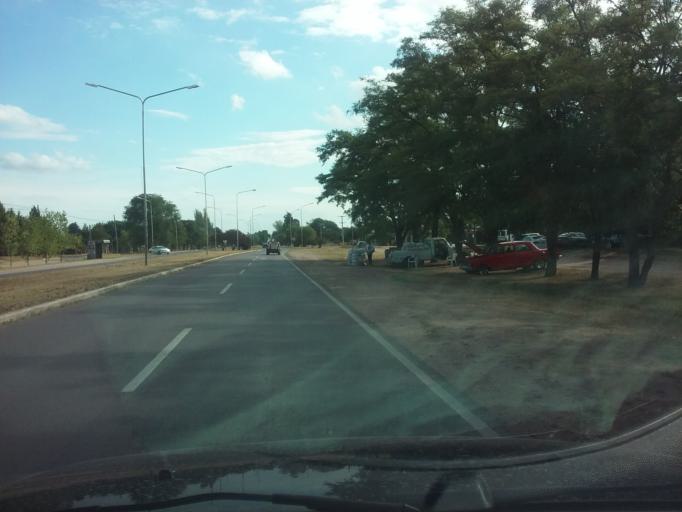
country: AR
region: La Pampa
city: Santa Rosa
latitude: -36.6373
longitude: -64.3188
